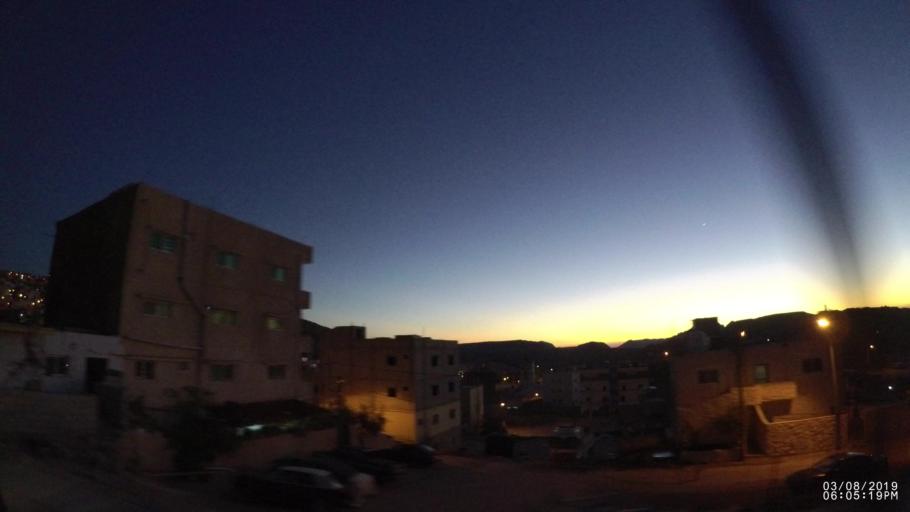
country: JO
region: Ma'an
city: Petra
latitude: 30.3280
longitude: 35.4715
